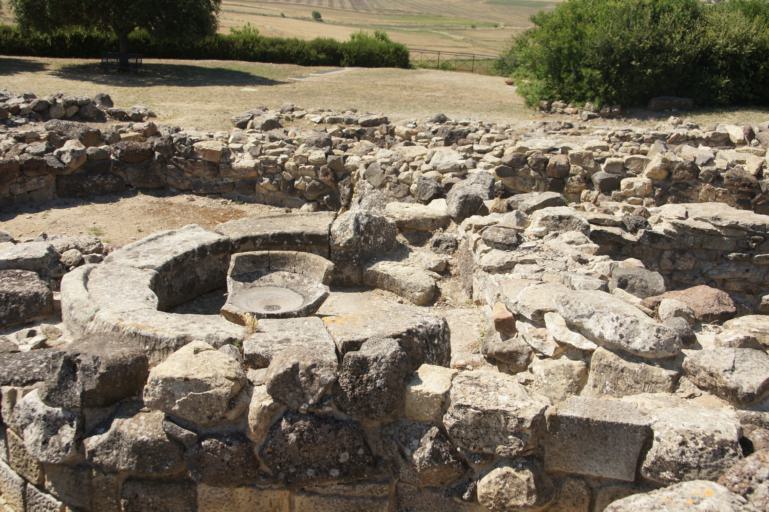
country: IT
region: Sardinia
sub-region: Provincia di Medio Campidano
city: Barumini
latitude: 39.7057
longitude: 8.9914
